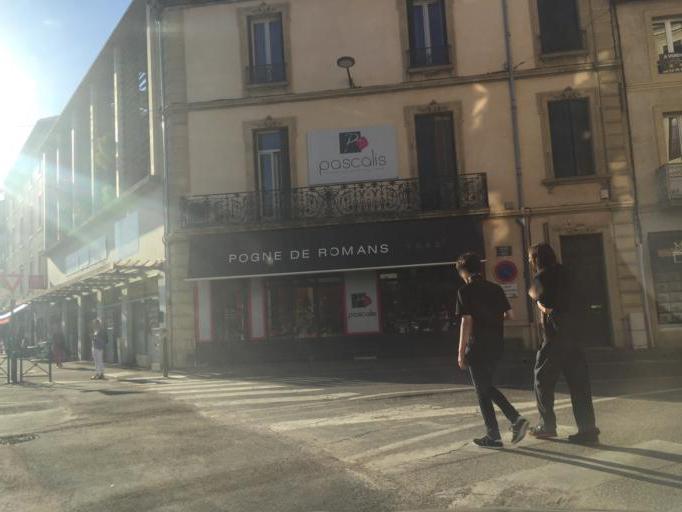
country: FR
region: Rhone-Alpes
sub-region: Departement de la Drome
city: Romans-sur-Isere
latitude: 45.0460
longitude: 5.0533
